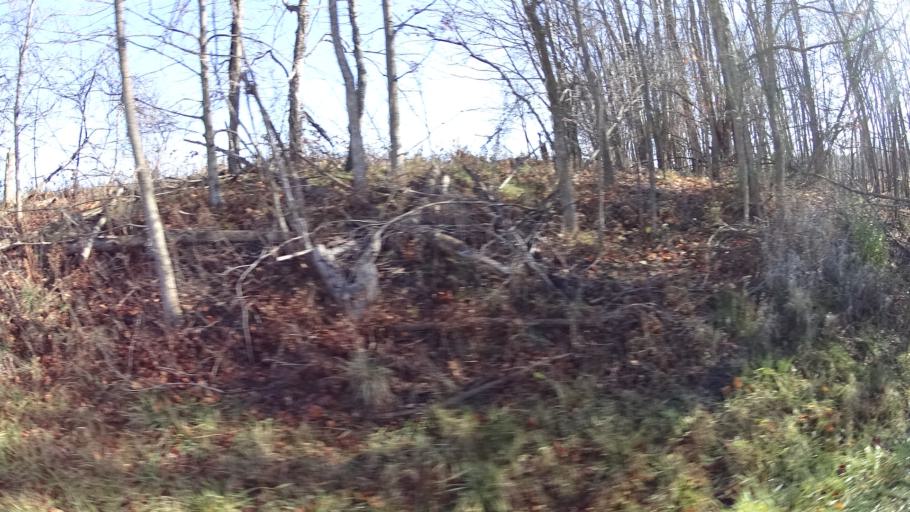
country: US
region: Ohio
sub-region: Lorain County
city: Wellington
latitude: 41.0839
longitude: -82.2793
